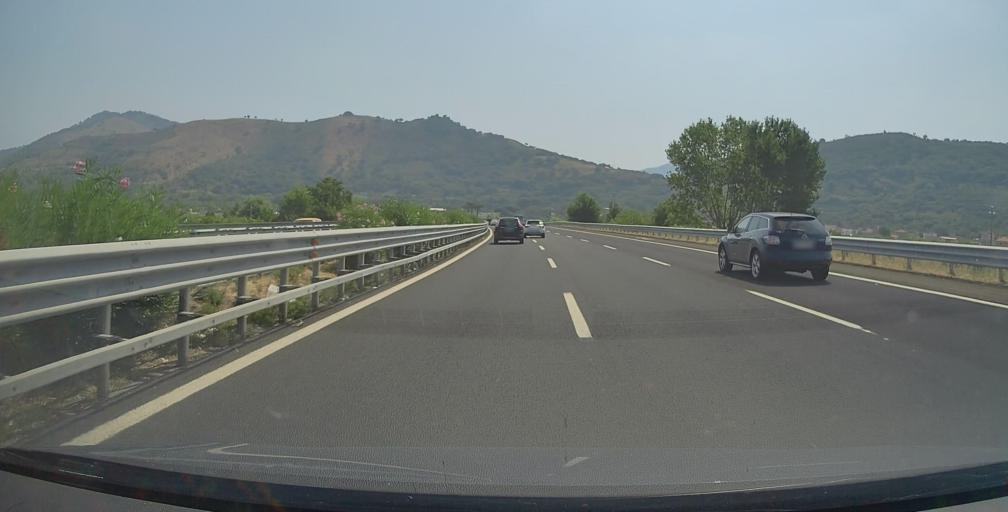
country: IT
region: Campania
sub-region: Provincia di Salerno
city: Nocera Inferiore
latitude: 40.7754
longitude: 14.6370
